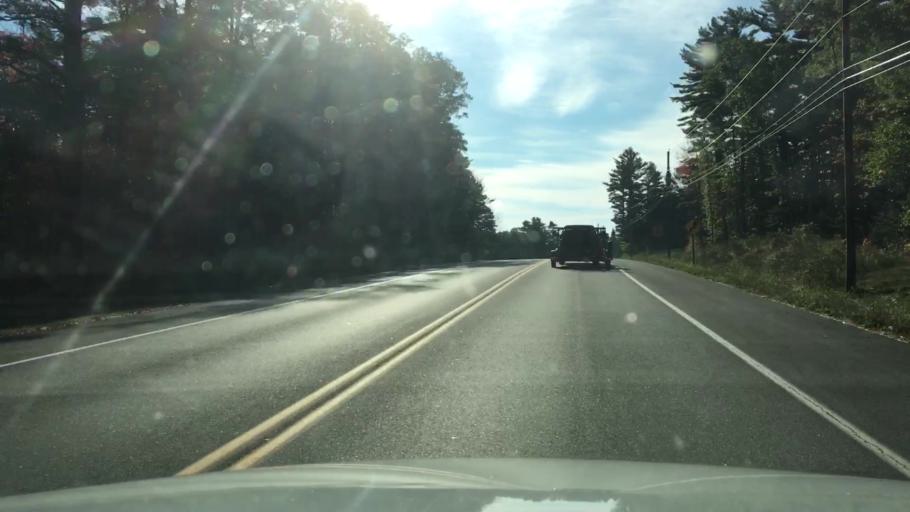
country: US
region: Maine
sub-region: Knox County
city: Warren
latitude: 44.0914
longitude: -69.2366
